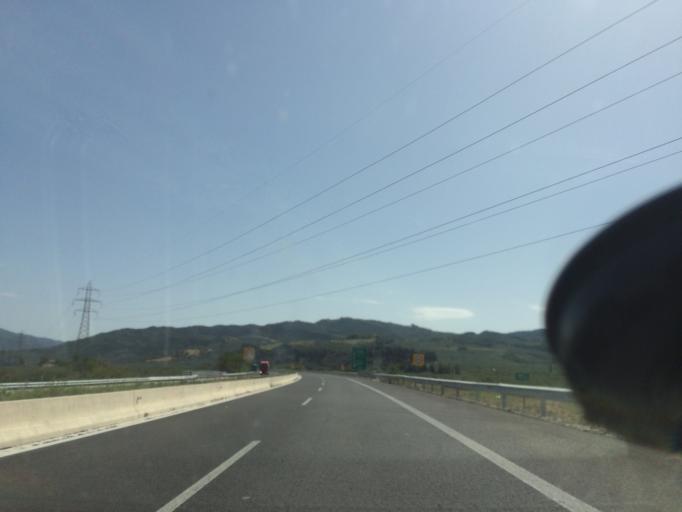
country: GR
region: Central Greece
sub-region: Nomos Fthiotidos
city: Molos
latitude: 38.8075
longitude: 22.6366
